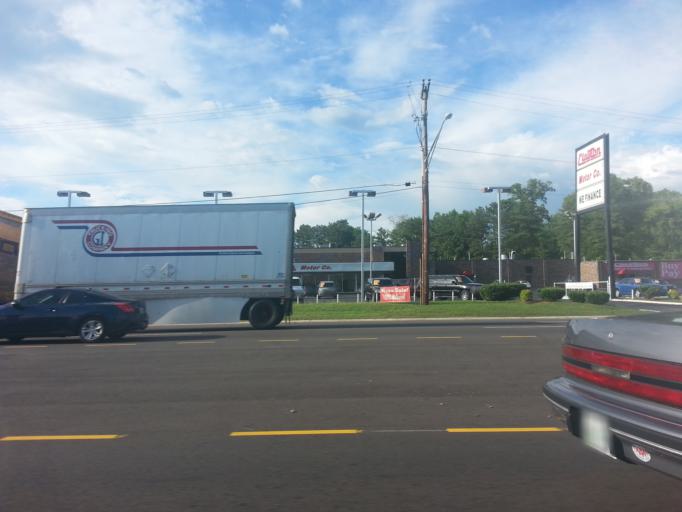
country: US
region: Tennessee
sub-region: Knox County
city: Knoxville
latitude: 36.0001
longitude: -83.9686
